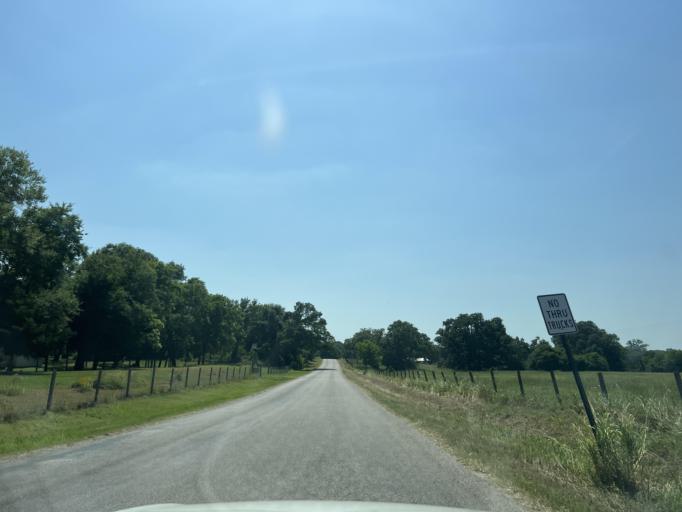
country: US
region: Texas
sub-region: Washington County
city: Brenham
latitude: 30.1599
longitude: -96.4544
